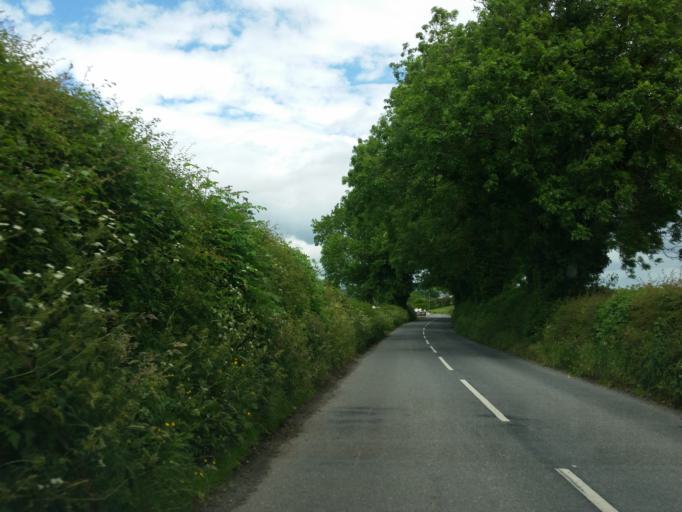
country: GB
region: Northern Ireland
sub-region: Omagh District
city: Omagh
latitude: 54.5456
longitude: -7.1159
